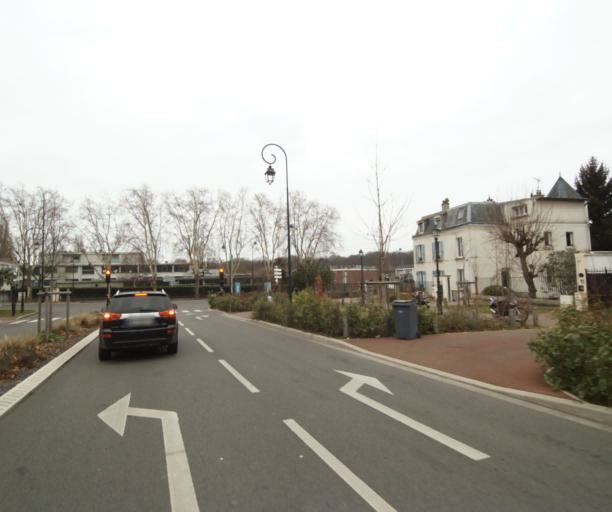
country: FR
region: Ile-de-France
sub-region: Departement des Hauts-de-Seine
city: Saint-Cloud
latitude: 48.8420
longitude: 2.1991
